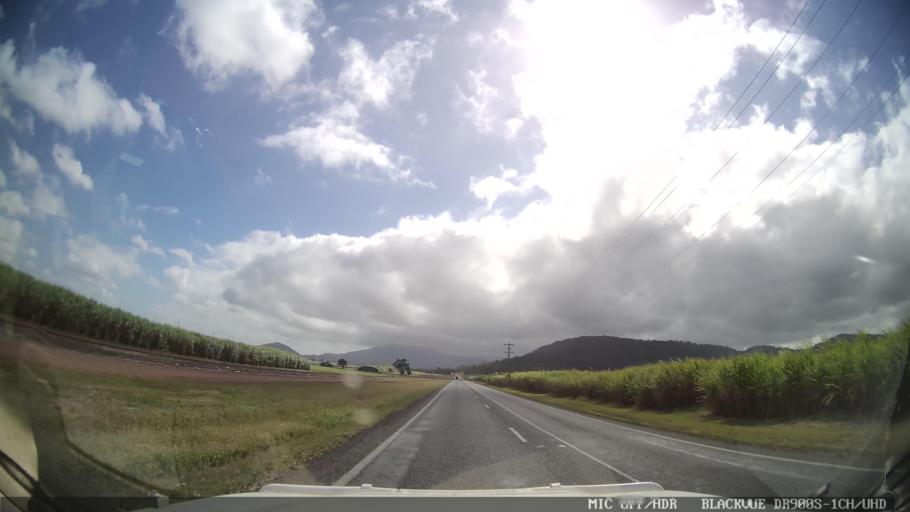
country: AU
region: Queensland
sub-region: Whitsunday
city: Red Hill
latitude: -20.3428
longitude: 148.5529
